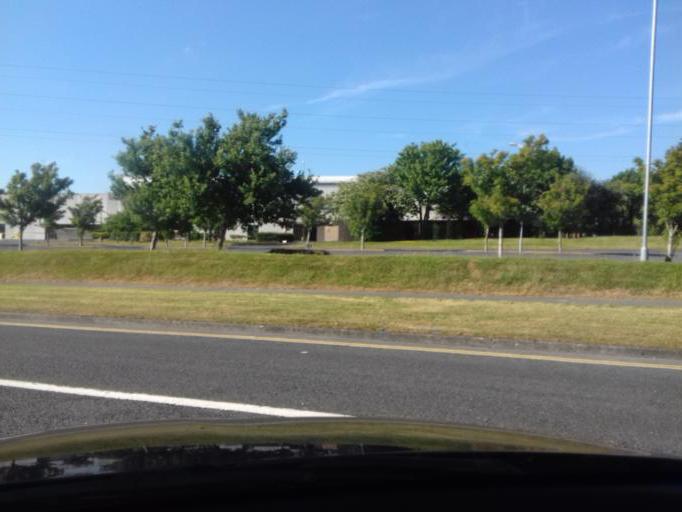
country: IE
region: Leinster
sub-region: Fingal County
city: Blanchardstown
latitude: 53.4039
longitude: -6.3705
